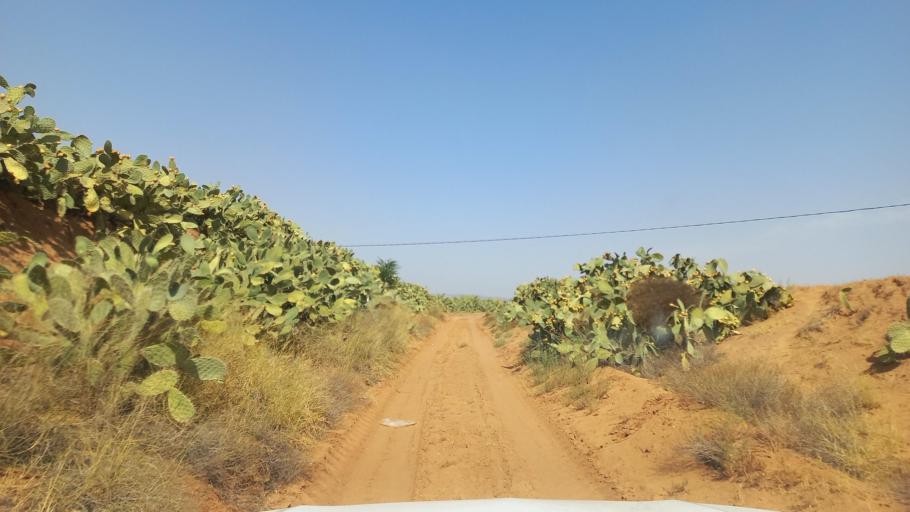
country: TN
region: Al Qasrayn
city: Kasserine
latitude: 35.2464
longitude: 9.0568
